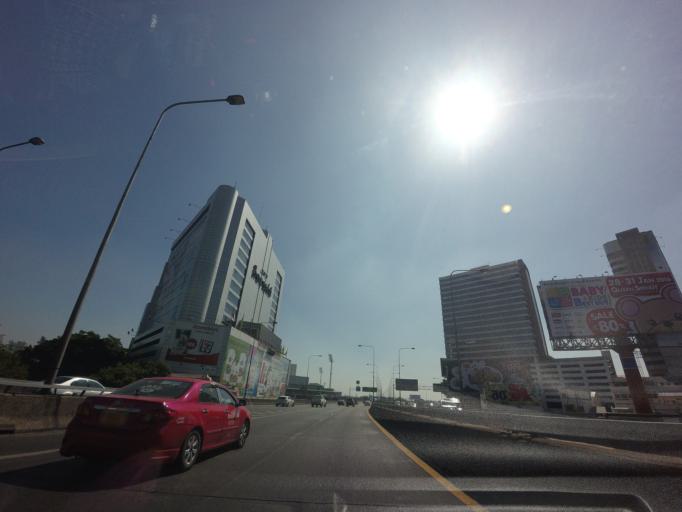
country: TH
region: Bangkok
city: Khlong Toei
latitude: 13.7161
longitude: 100.5571
